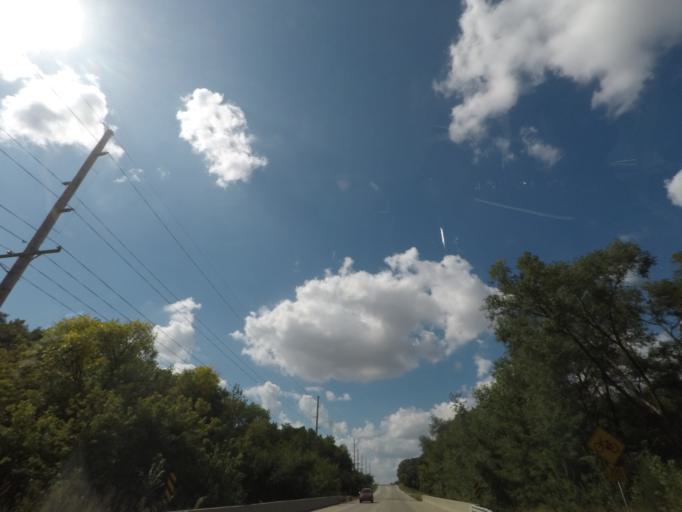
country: US
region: Iowa
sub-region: Story County
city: Nevada
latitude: 42.0228
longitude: -93.4677
